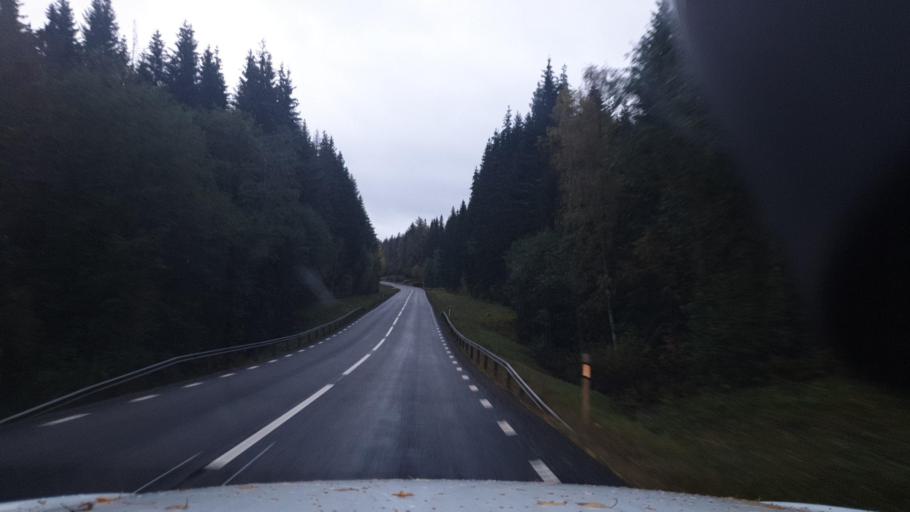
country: SE
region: Vaermland
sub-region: Eda Kommun
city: Amotfors
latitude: 59.8014
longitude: 12.3265
